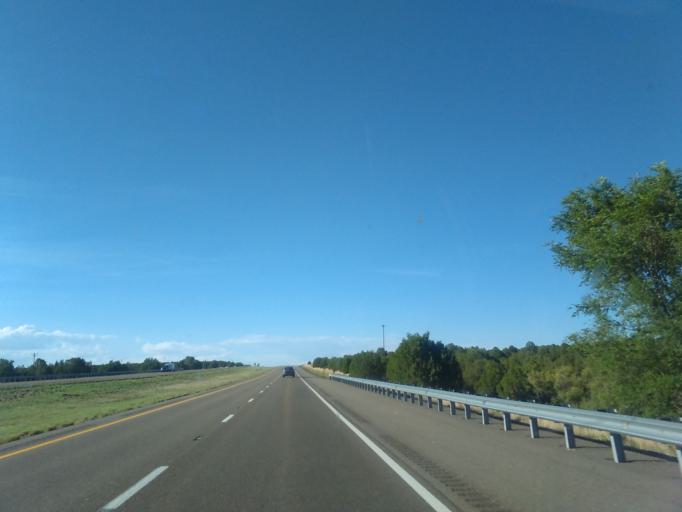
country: US
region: New Mexico
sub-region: San Miguel County
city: Las Vegas
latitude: 35.4714
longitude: -105.2754
